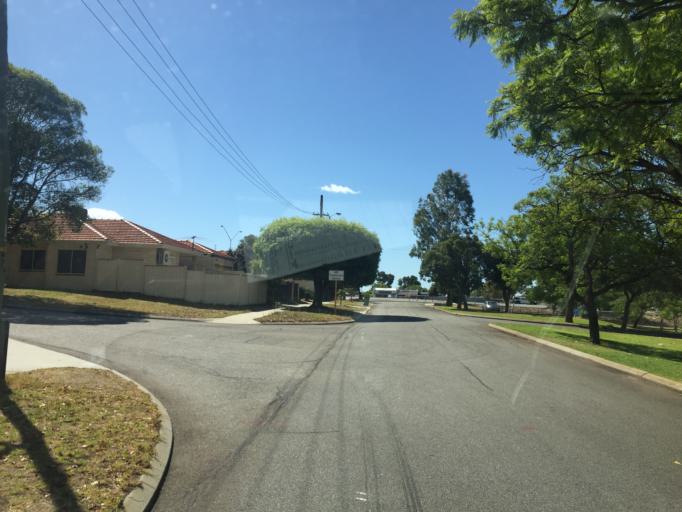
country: AU
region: Western Australia
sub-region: Belmont
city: Redcliffe
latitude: -31.9348
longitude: 115.9396
